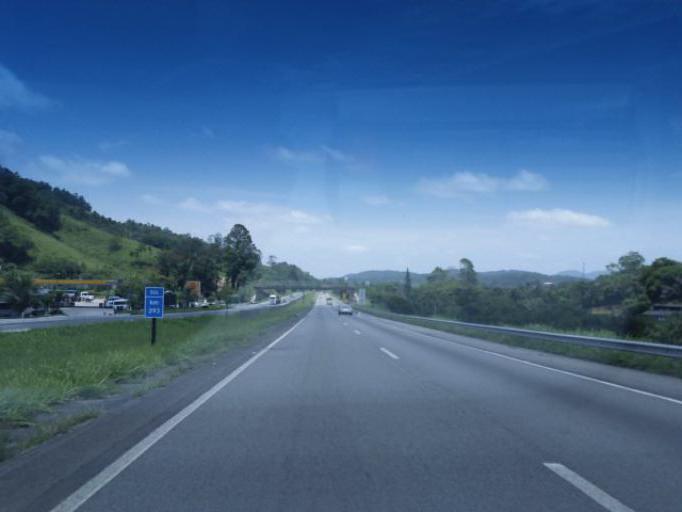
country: BR
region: Sao Paulo
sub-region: Miracatu
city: Miracatu
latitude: -24.2854
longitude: -47.4423
